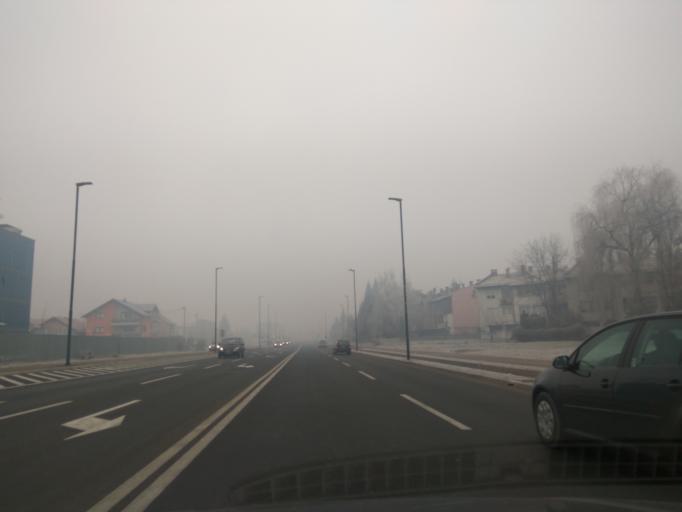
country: BA
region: Federation of Bosnia and Herzegovina
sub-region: Kanton Sarajevo
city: Sarajevo
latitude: 43.8291
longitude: 18.3347
